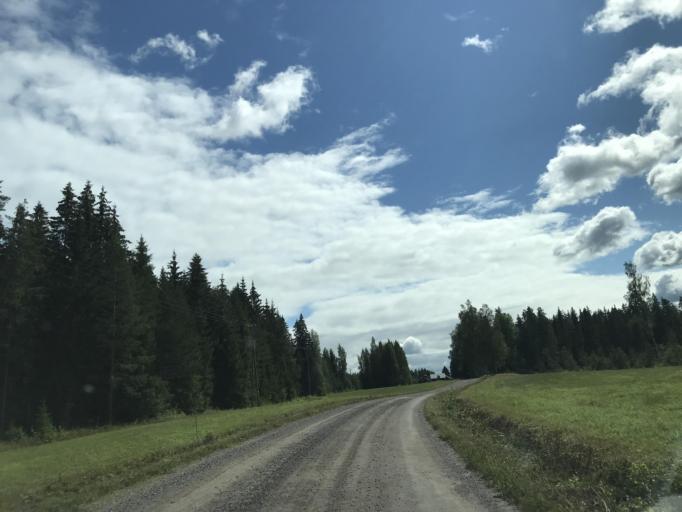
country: FI
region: Uusimaa
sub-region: Helsinki
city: Kaerkoelae
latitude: 60.6335
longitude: 23.8351
